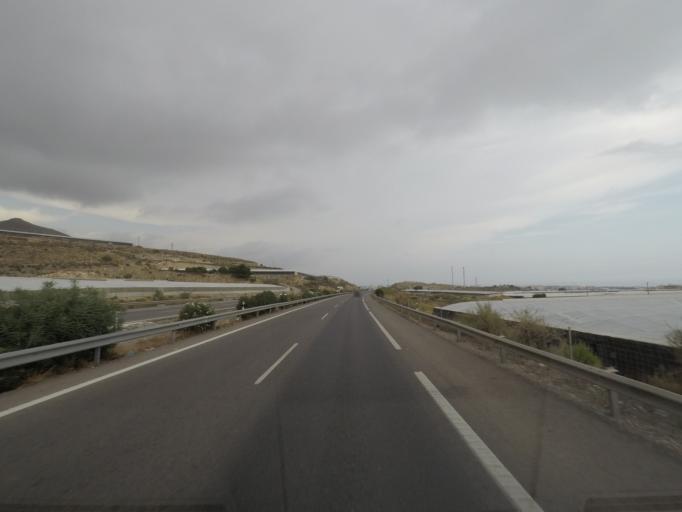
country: ES
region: Andalusia
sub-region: Provincia de Almeria
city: Vicar
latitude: 36.8124
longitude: -2.6226
